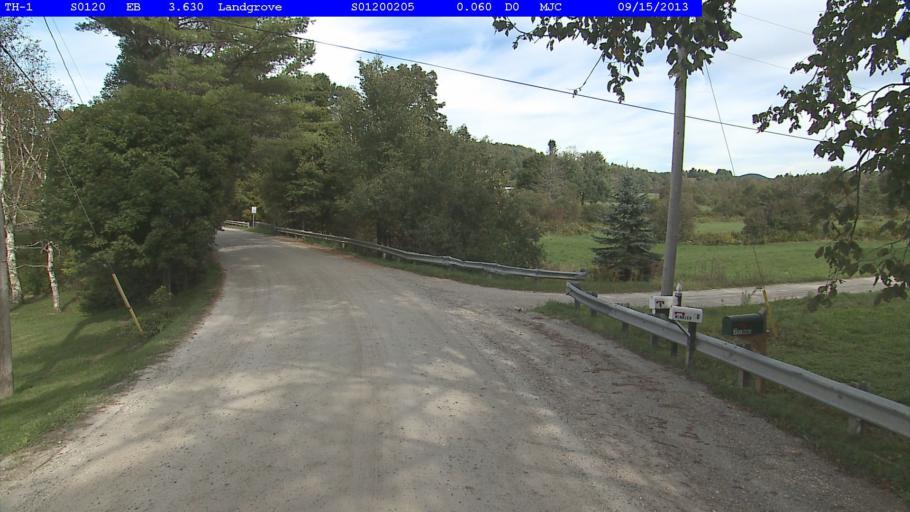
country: US
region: Vermont
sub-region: Bennington County
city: Manchester Center
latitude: 43.2630
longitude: -72.8621
